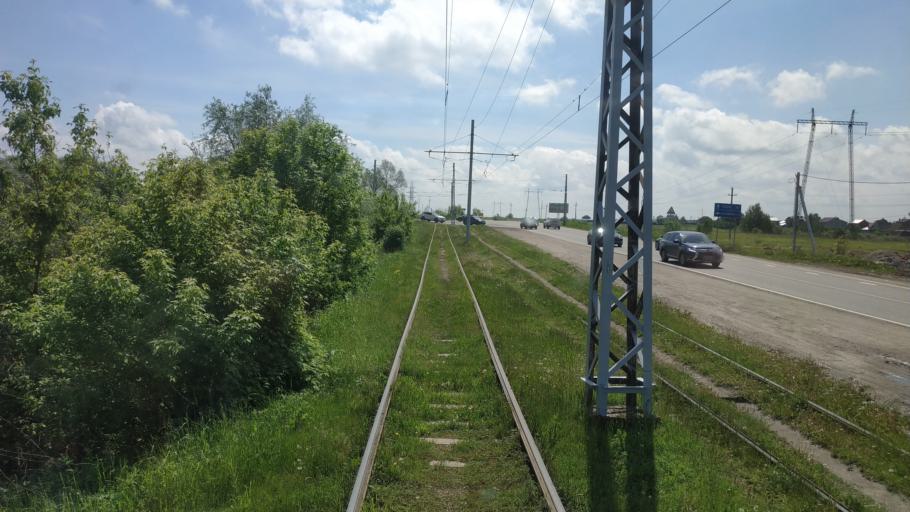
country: RU
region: Moskovskaya
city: Sychevo
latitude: 55.0606
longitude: 38.7268
